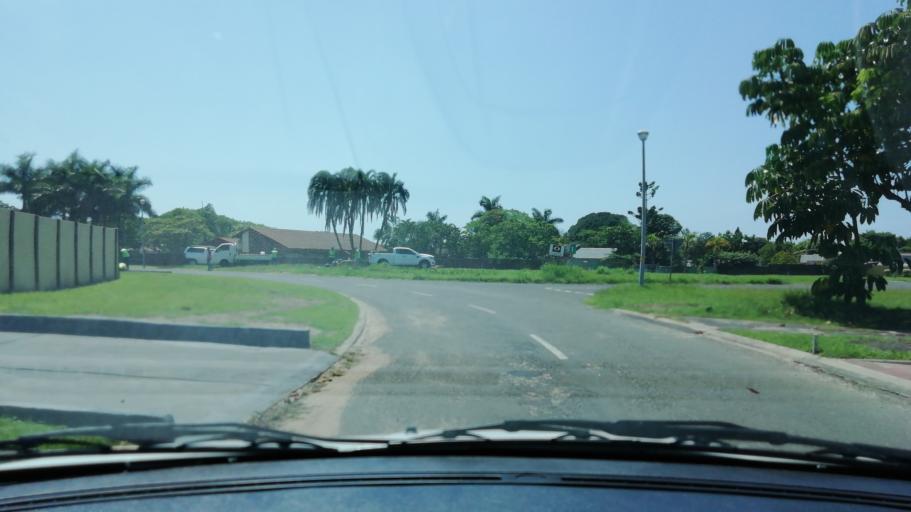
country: ZA
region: KwaZulu-Natal
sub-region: uThungulu District Municipality
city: Richards Bay
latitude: -28.7408
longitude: 32.0582
